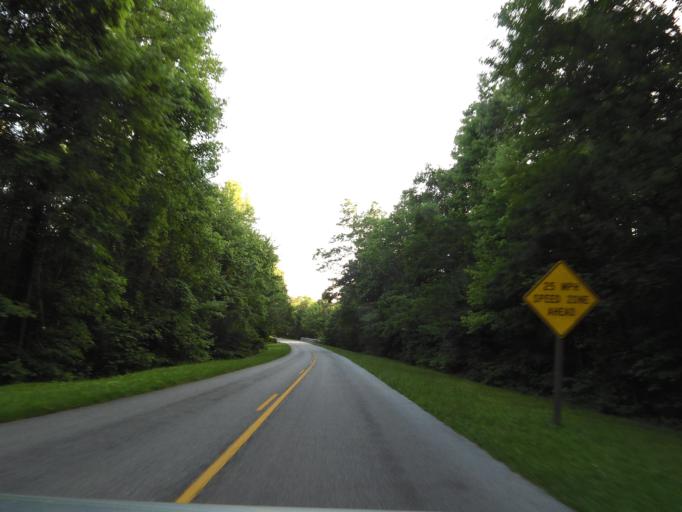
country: US
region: Tennessee
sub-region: Blount County
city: Maryville
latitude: 35.6386
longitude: -83.9367
